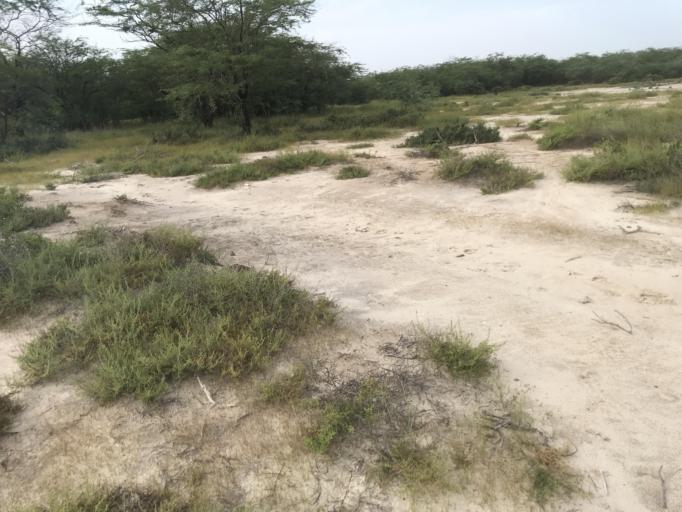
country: SN
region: Saint-Louis
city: Saint-Louis
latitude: 15.9281
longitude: -16.4665
